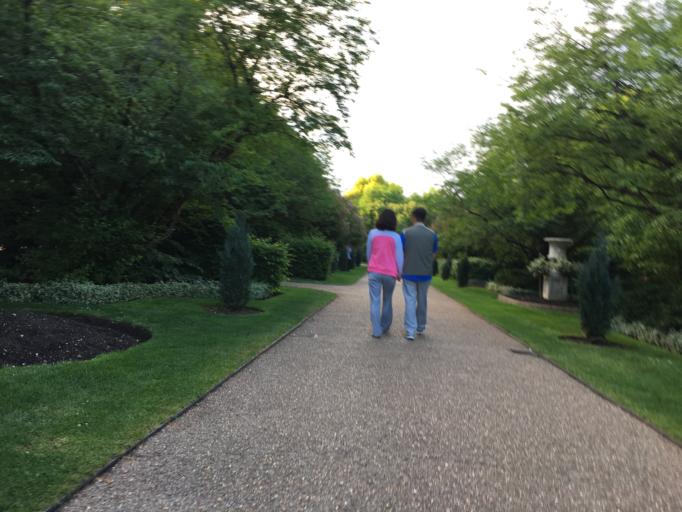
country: GB
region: England
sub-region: Greater London
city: Camden Town
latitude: 51.5274
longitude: -0.1479
